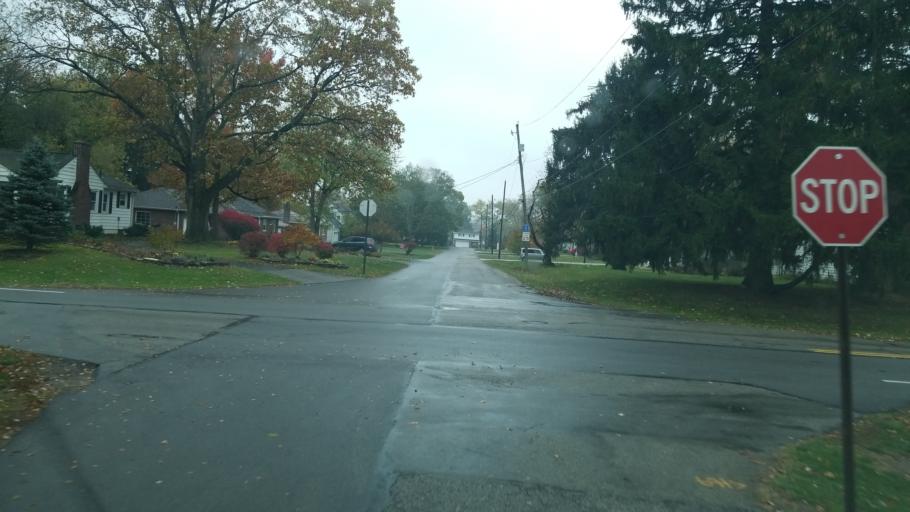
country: US
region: Ohio
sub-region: Franklin County
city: Upper Arlington
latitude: 40.0400
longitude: -83.0447
